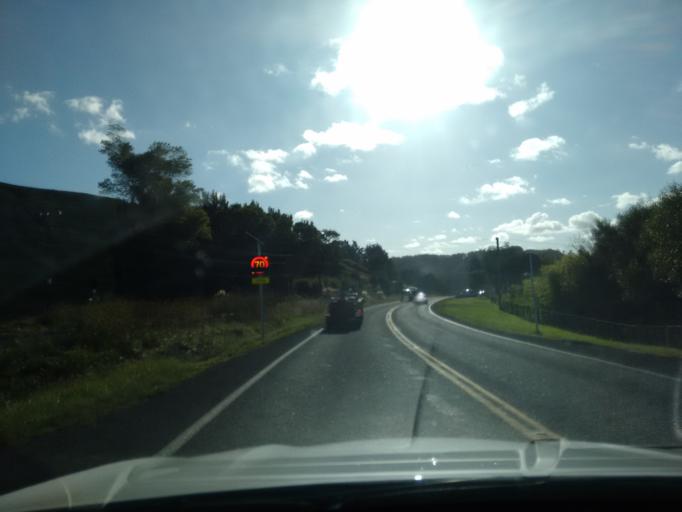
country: NZ
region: Manawatu-Wanganui
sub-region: Wanganui District
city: Wanganui
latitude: -39.8523
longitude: 174.9334
